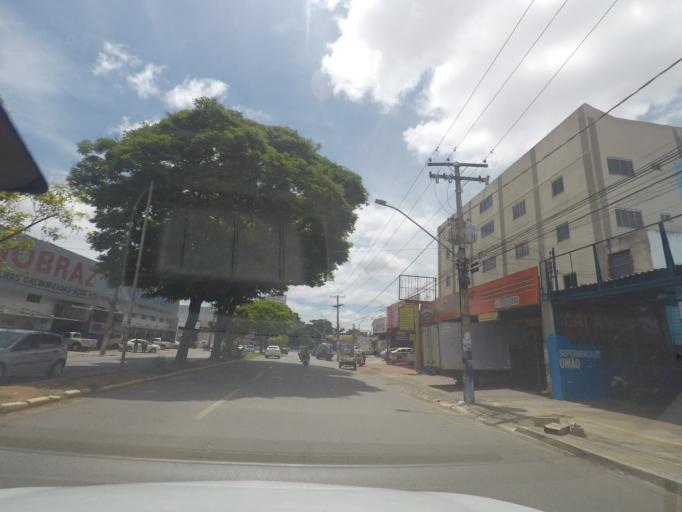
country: BR
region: Goias
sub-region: Goiania
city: Goiania
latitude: -16.6601
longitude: -49.2466
